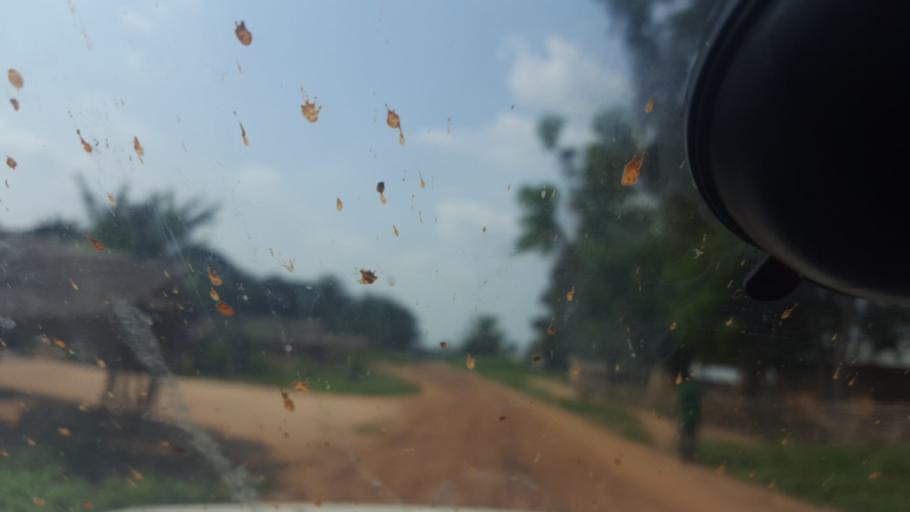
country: CD
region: Bandundu
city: Bandundu
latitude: -3.7494
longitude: 17.0380
